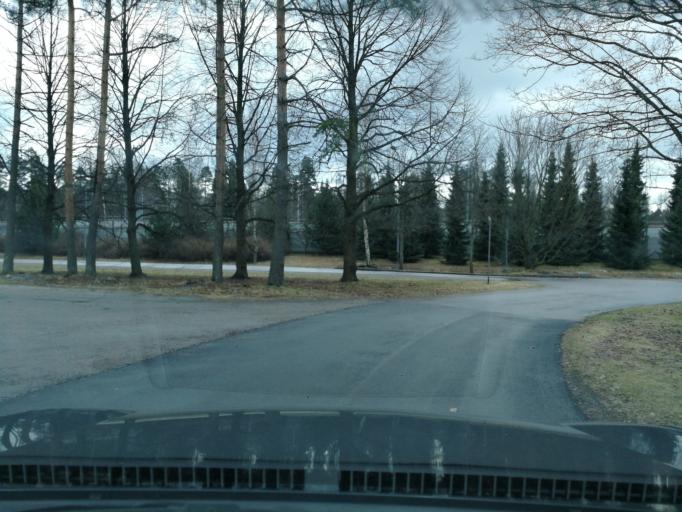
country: FI
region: Uusimaa
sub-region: Helsinki
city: Koukkuniemi
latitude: 60.1696
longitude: 24.7936
